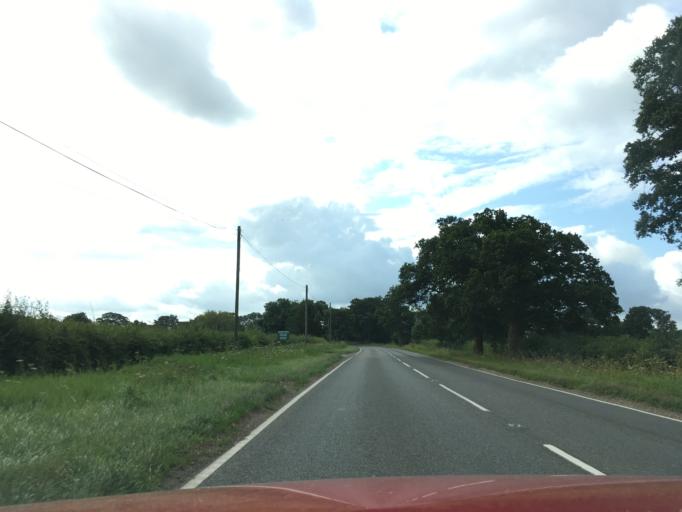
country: GB
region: England
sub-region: Hampshire
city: Colden Common
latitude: 50.9781
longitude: -1.2650
